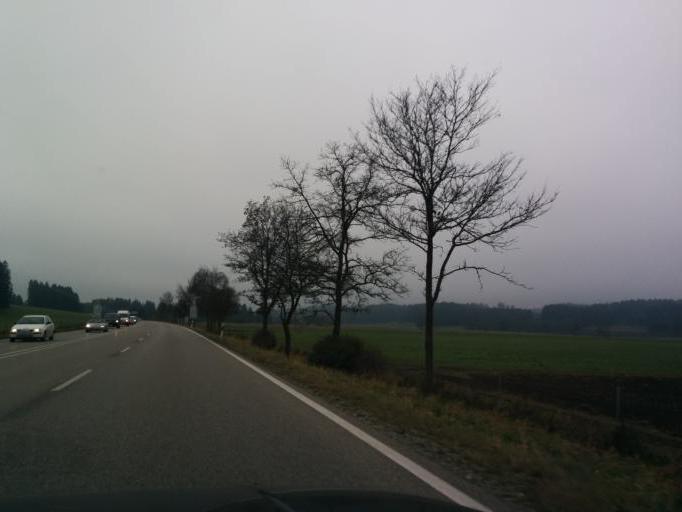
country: DE
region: Bavaria
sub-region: Swabia
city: Ruderatshofen
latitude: 47.7941
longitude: 10.5854
